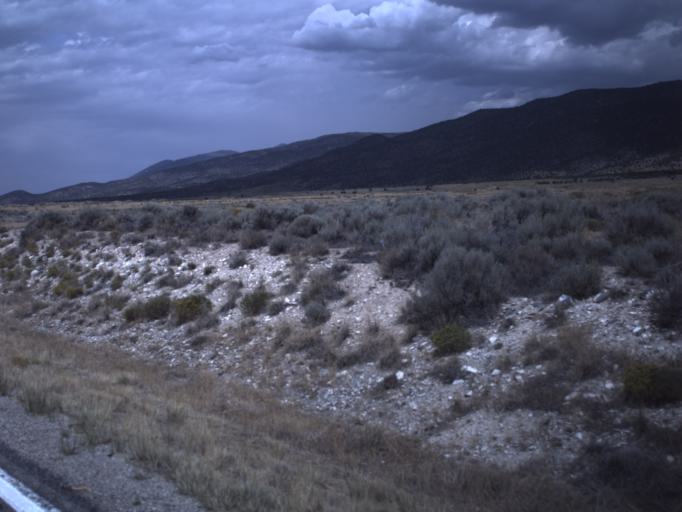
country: US
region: Utah
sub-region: Utah County
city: Eagle Mountain
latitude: 40.2579
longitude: -112.2277
